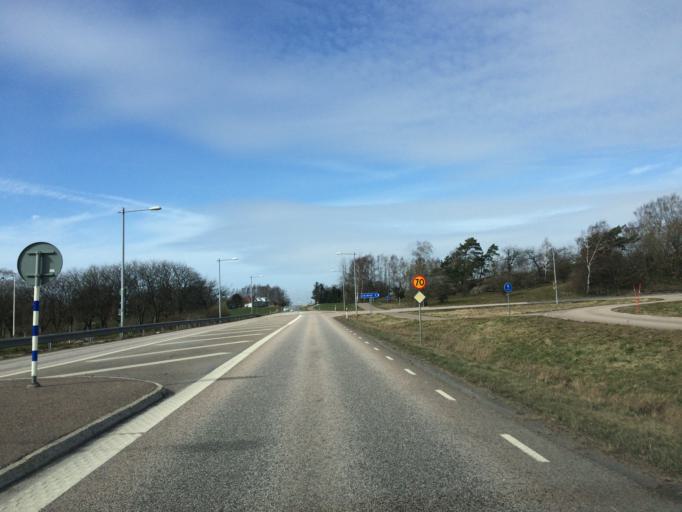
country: SE
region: Halland
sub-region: Laholms Kommun
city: Veinge
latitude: 56.5557
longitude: 13.0392
